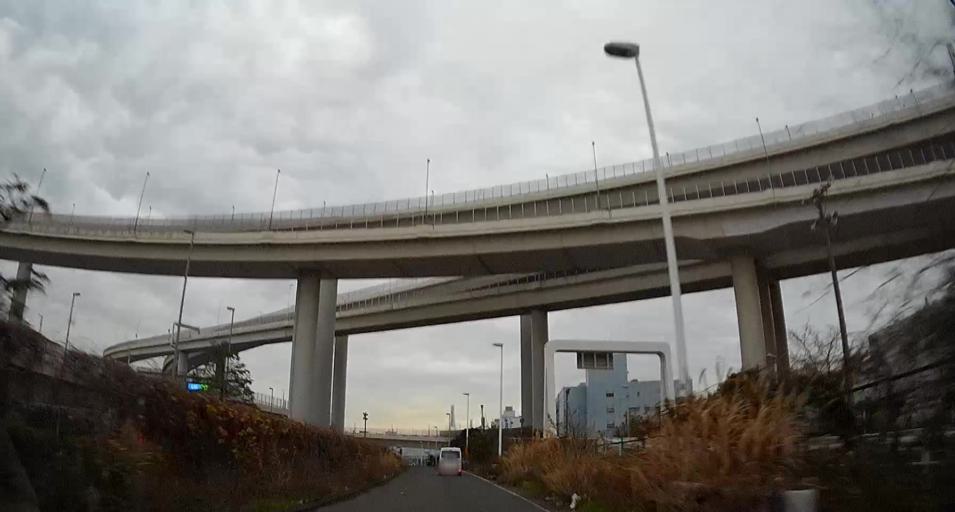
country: JP
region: Kanagawa
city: Yokohama
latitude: 35.4619
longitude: 139.6817
